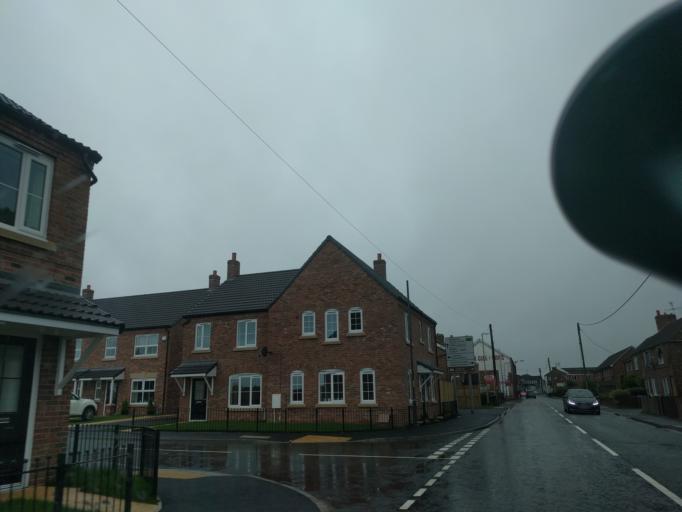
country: GB
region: England
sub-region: North Yorkshire
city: Bedale
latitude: 54.3060
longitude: -1.5574
